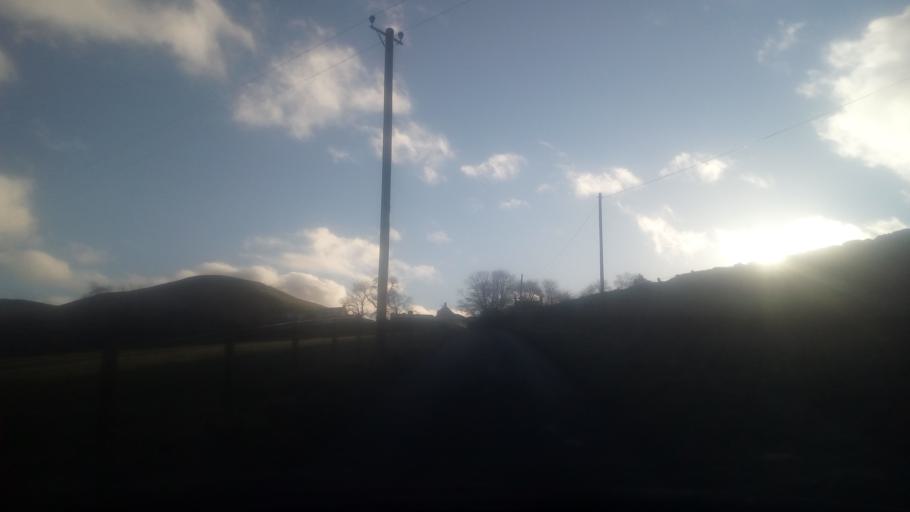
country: GB
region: Scotland
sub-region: The Scottish Borders
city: Kelso
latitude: 55.4511
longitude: -2.3677
